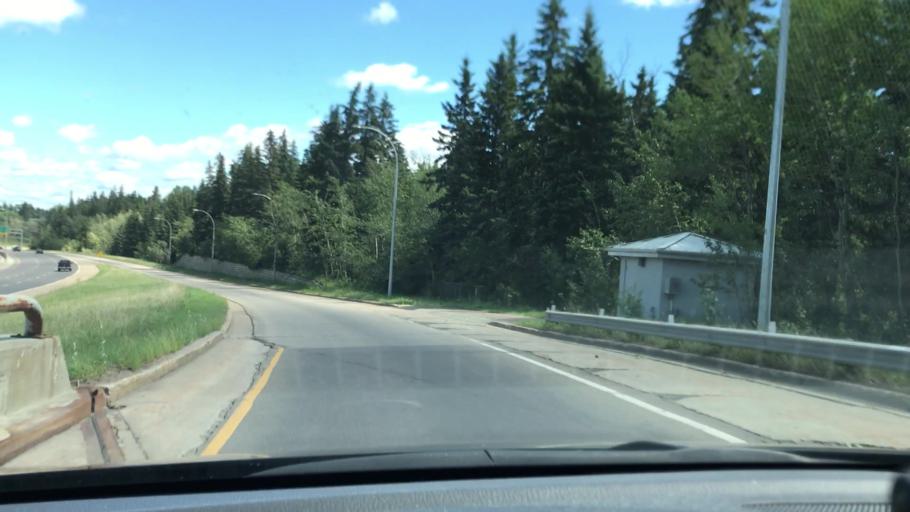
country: CA
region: Alberta
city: Edmonton
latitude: 53.5117
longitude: -113.5786
